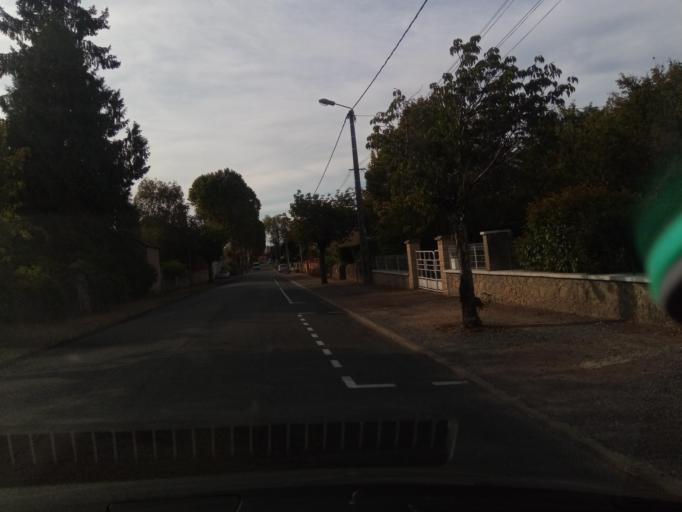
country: FR
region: Poitou-Charentes
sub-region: Departement de la Vienne
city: Montmorillon
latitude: 46.4193
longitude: 0.8775
